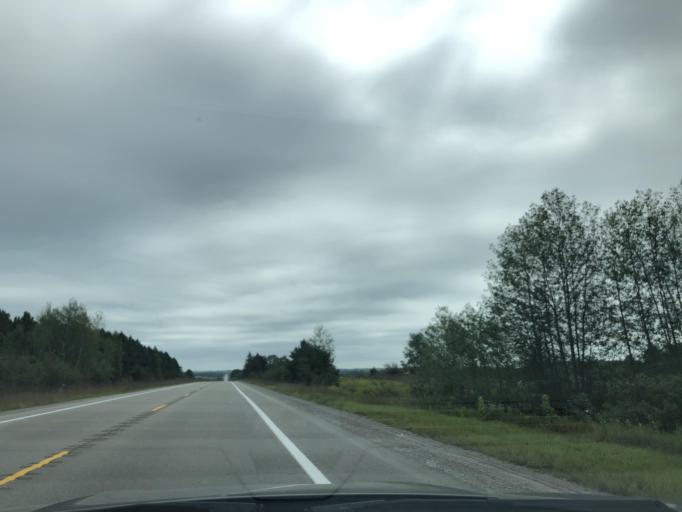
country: US
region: Michigan
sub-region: Clare County
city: Harrison
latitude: 44.0311
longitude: -84.9586
